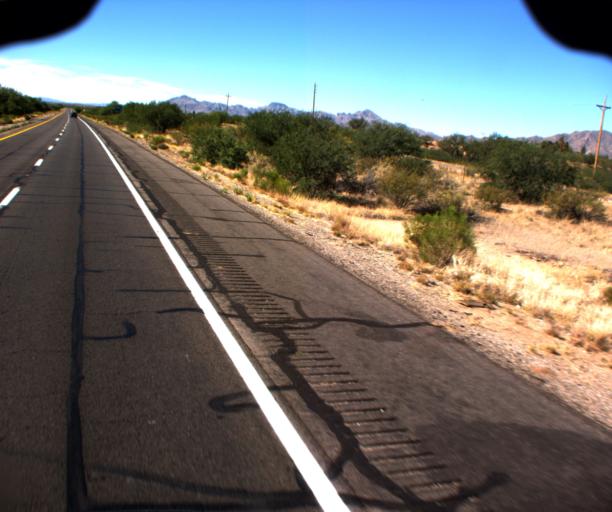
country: US
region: Arizona
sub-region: Pima County
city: Arivaca Junction
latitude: 31.7009
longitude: -111.0657
